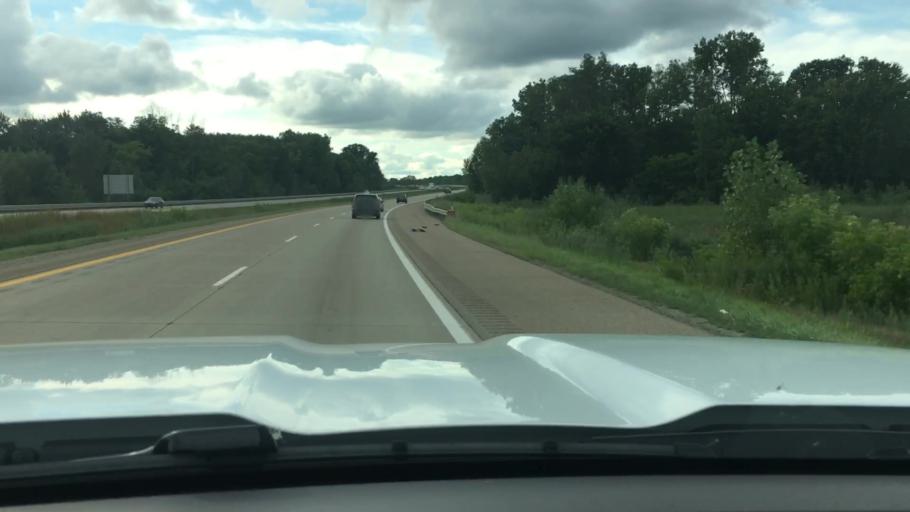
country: US
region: Michigan
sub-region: Kent County
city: Kentwood
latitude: 42.8473
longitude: -85.5696
